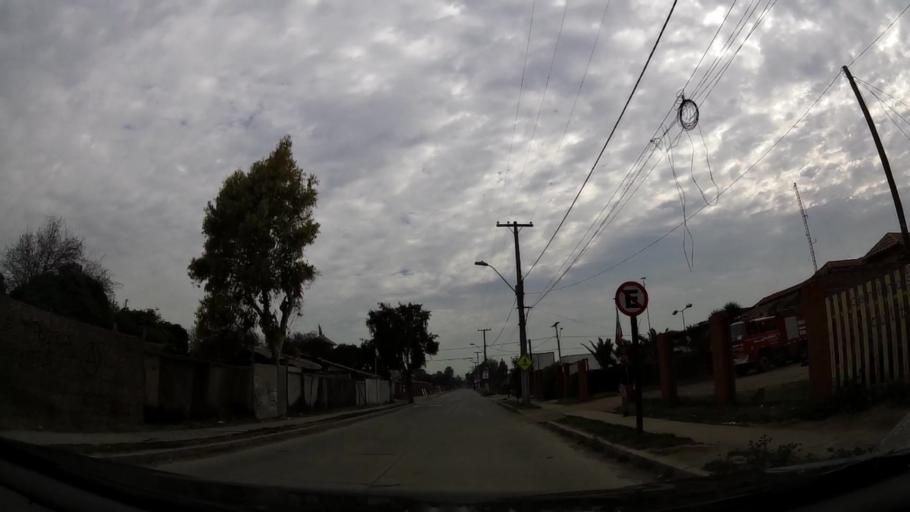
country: CL
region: Santiago Metropolitan
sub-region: Provincia de Chacabuco
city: Lampa
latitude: -33.2296
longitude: -70.8130
